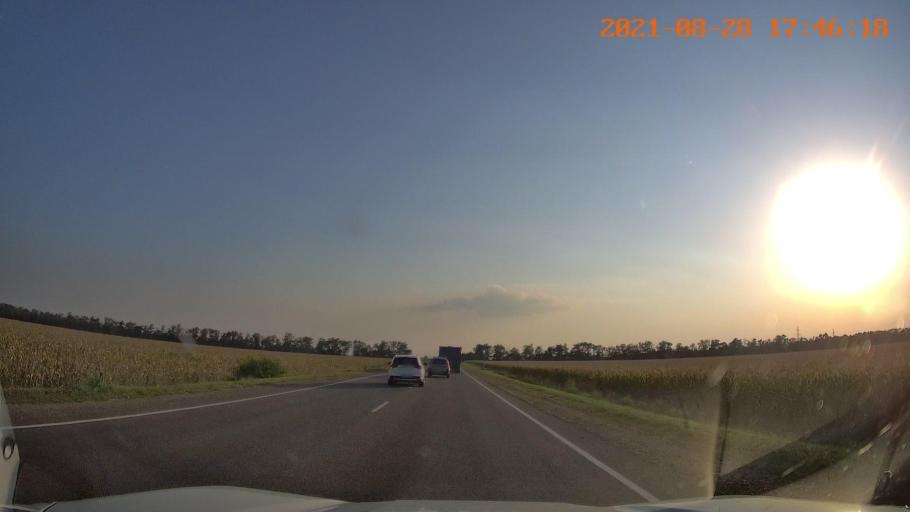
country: RU
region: Krasnodarskiy
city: Glubokiy
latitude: 44.9804
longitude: 40.8638
